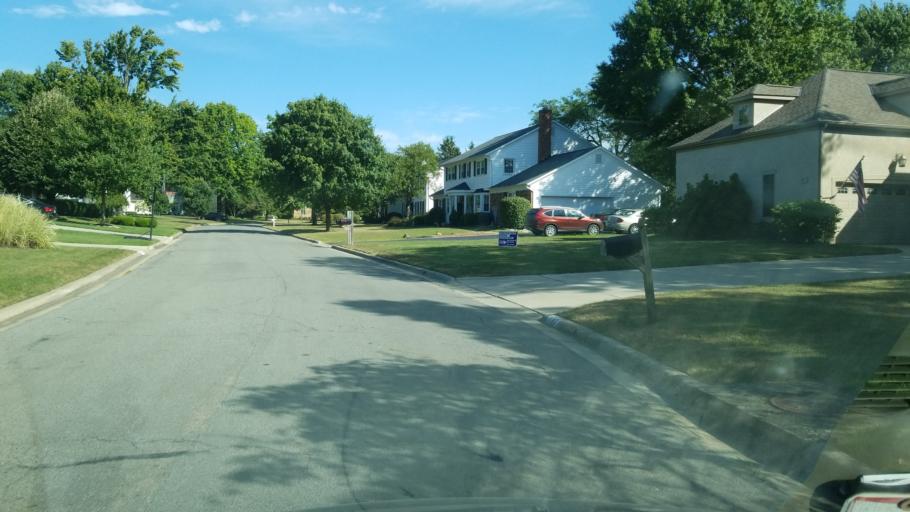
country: US
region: Ohio
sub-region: Franklin County
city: Worthington
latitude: 40.1267
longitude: -83.0448
